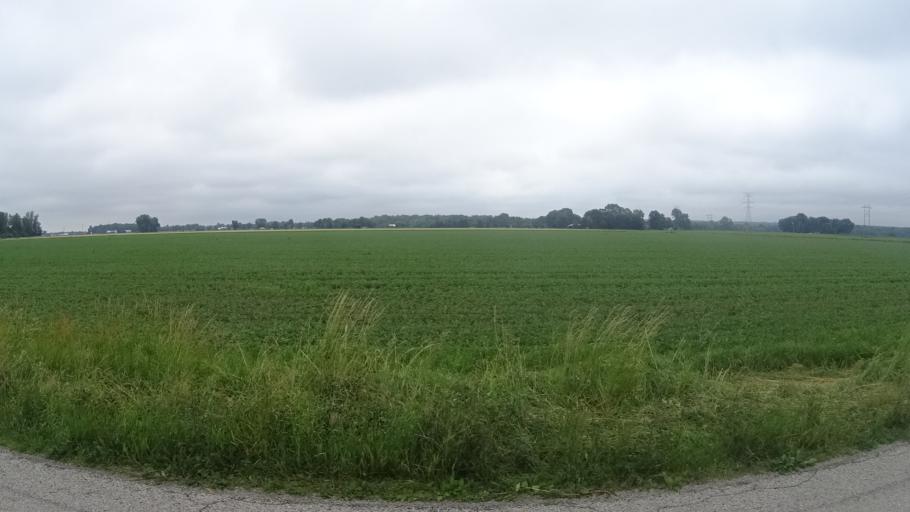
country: US
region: Ohio
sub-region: Erie County
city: Huron
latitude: 41.3385
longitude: -82.5438
